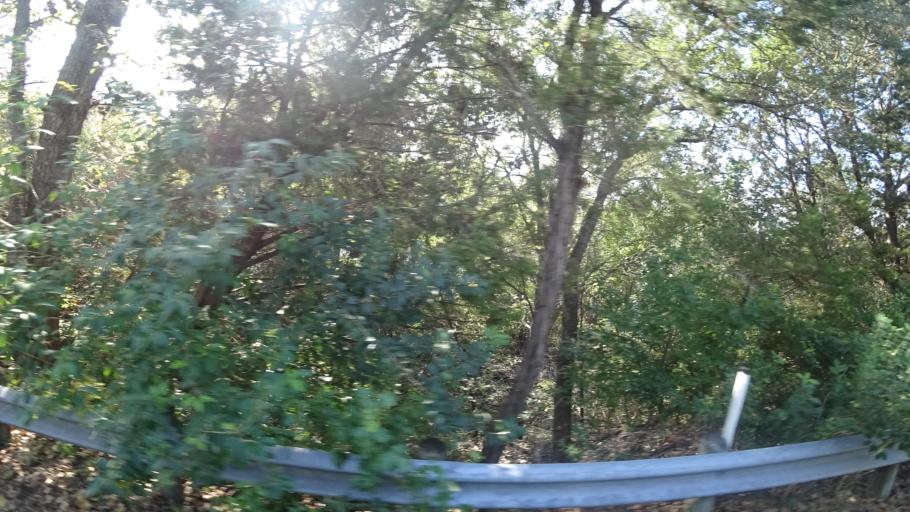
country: US
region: Texas
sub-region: Travis County
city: Lost Creek
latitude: 30.3170
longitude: -97.8649
